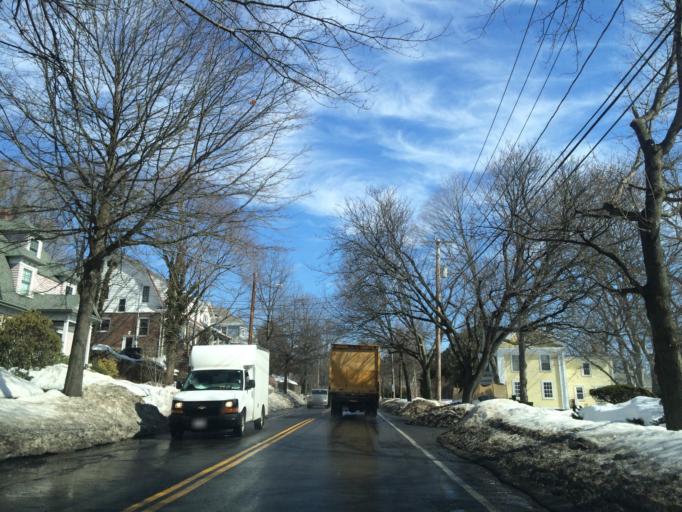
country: US
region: Massachusetts
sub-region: Middlesex County
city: Arlington
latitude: 42.4081
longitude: -71.1603
